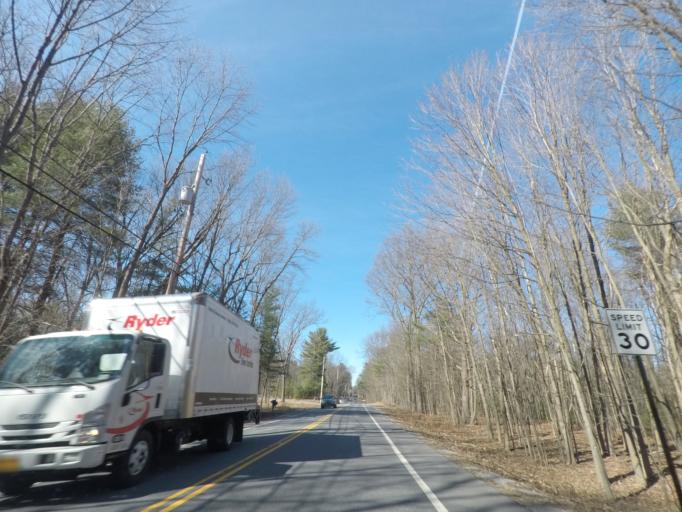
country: US
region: New York
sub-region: Saratoga County
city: North Ballston Spa
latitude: 43.0182
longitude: -73.8488
